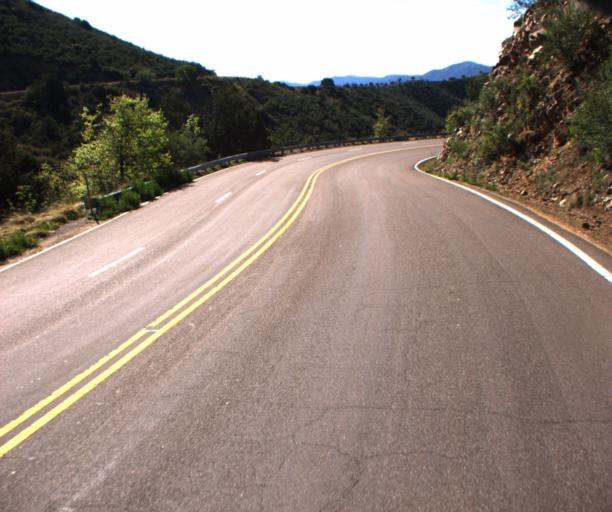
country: US
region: Arizona
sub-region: Yavapai County
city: Prescott
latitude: 34.4748
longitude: -112.5179
